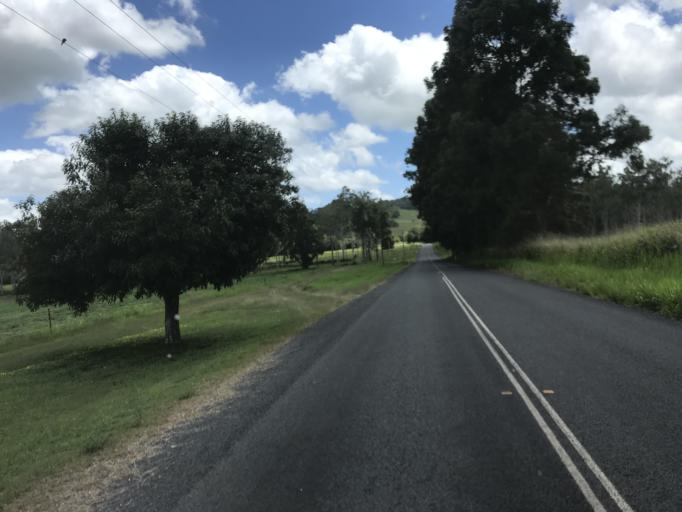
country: AU
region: Queensland
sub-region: Tablelands
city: Atherton
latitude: -17.3011
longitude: 145.5579
